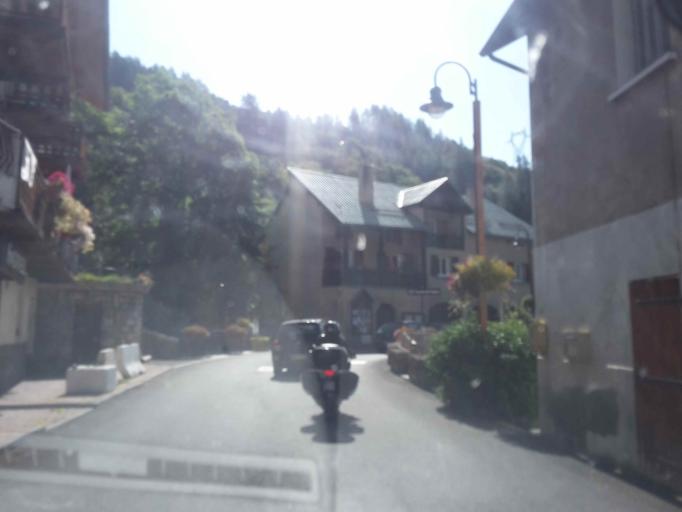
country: FR
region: Provence-Alpes-Cote d'Azur
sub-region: Departement des Hautes-Alpes
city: Guillestre
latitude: 44.6100
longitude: 6.6881
